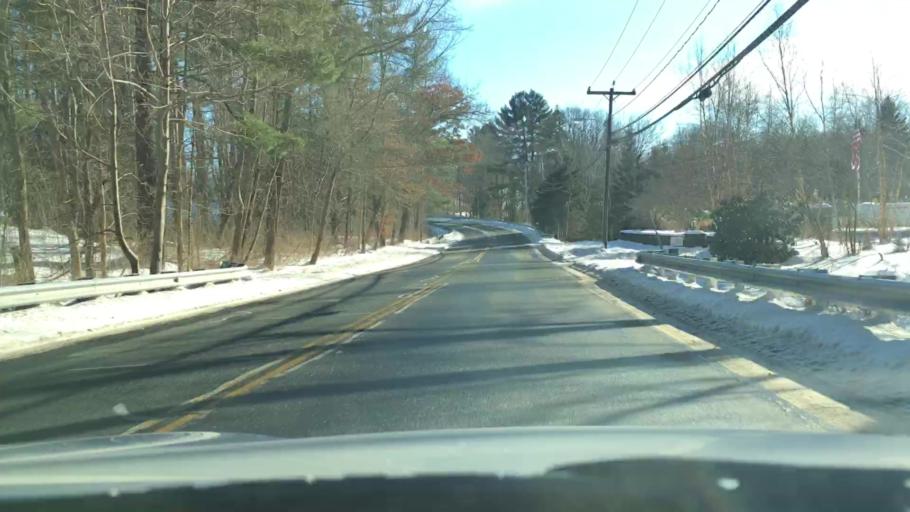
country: US
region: Massachusetts
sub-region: Hampden County
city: Longmeadow
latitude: 42.0439
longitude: -72.5721
